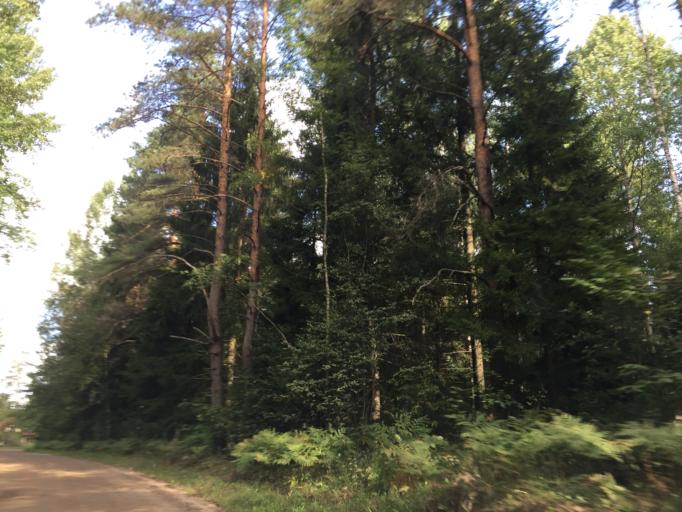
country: LV
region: Incukalns
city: Vangazi
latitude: 57.0894
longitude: 24.5636
